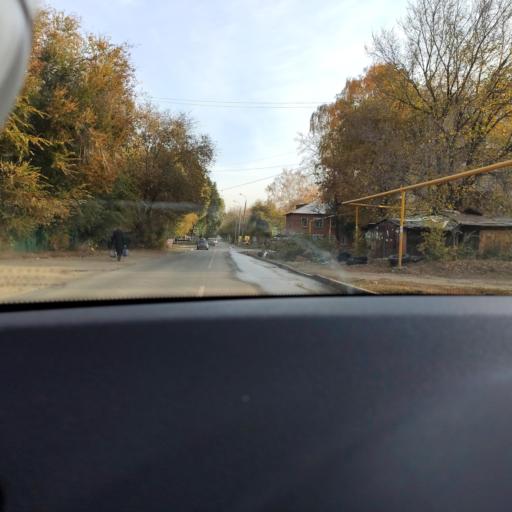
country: RU
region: Samara
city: Samara
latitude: 53.2225
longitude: 50.2270
